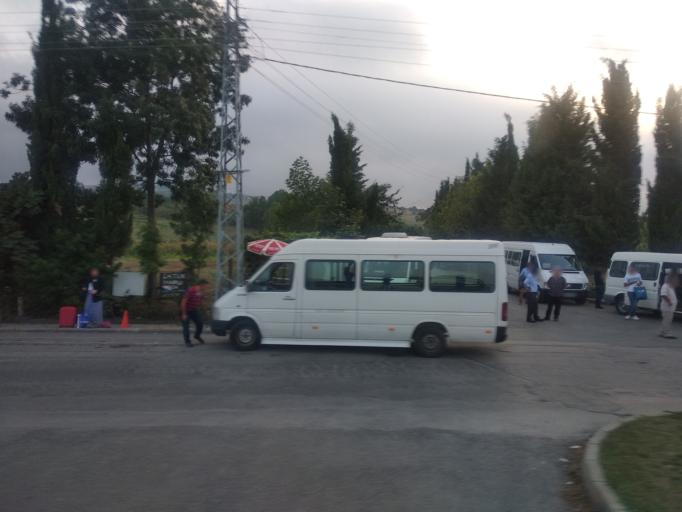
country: TR
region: Samsun
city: Samsun
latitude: 41.2870
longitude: 36.2878
